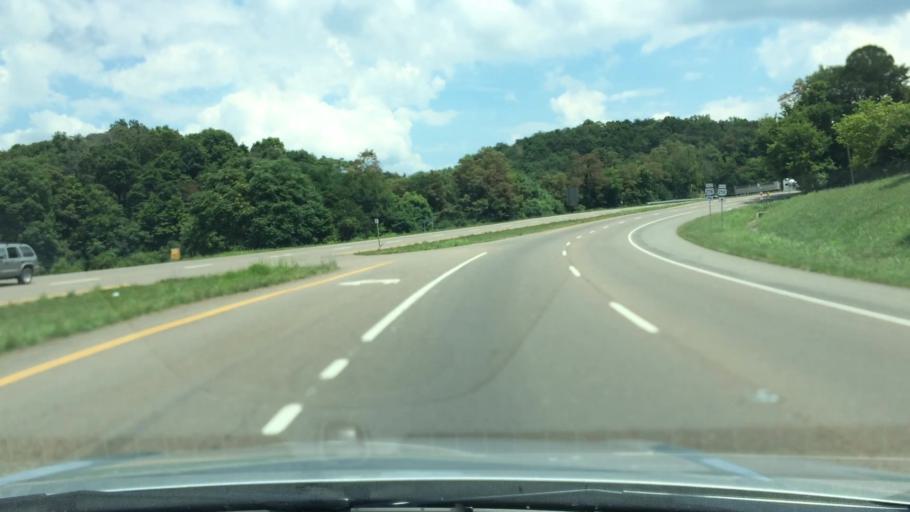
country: US
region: Tennessee
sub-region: Hamblen County
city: Morristown
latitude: 36.1935
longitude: -83.2726
